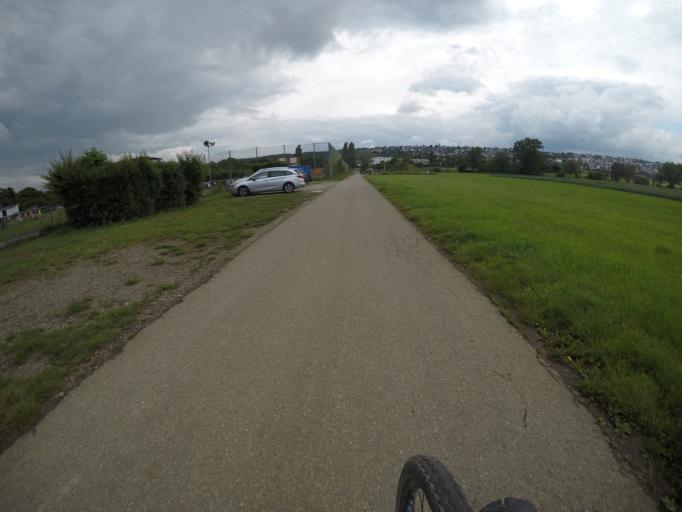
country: DE
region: Baden-Wuerttemberg
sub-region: Regierungsbezirk Stuttgart
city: Leinfelden-Echterdingen
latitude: 48.6774
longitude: 9.1829
